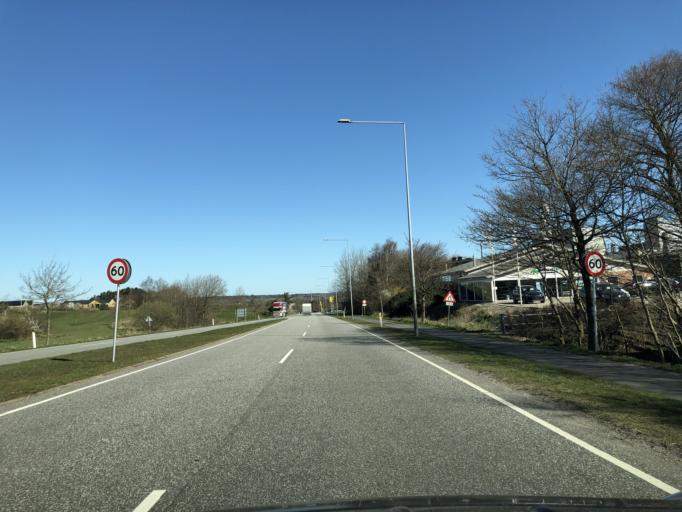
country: DK
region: North Denmark
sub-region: Rebild Kommune
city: Stovring
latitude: 56.8721
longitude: 9.8383
